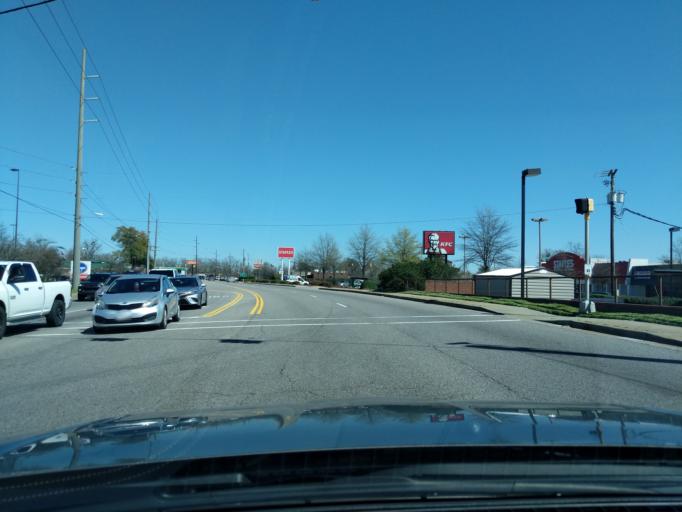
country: US
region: South Carolina
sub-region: Aiken County
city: Aiken
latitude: 33.5226
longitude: -81.7220
